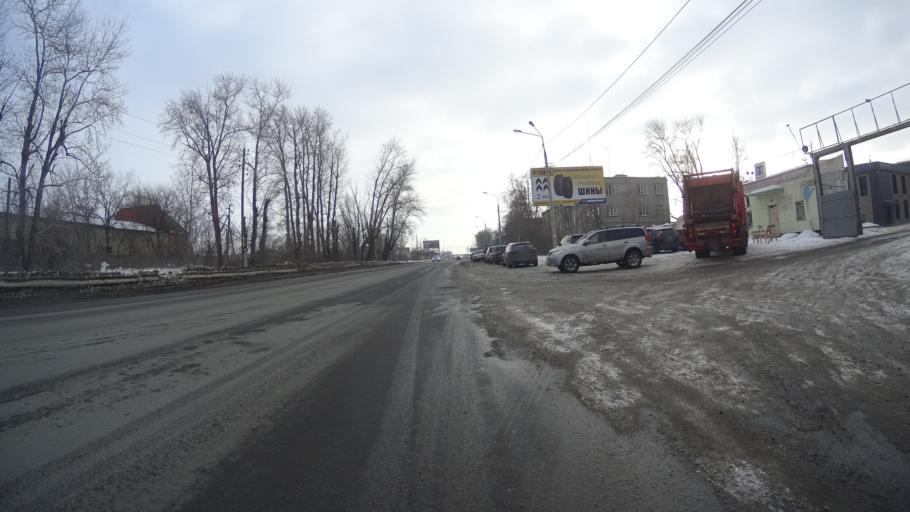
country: RU
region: Chelyabinsk
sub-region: Gorod Chelyabinsk
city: Chelyabinsk
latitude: 55.1241
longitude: 61.3858
